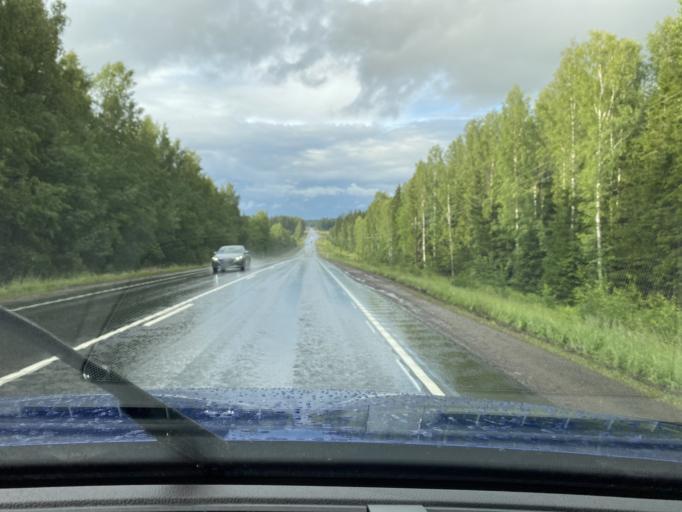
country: FI
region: Uusimaa
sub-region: Helsinki
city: Nurmijaervi
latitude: 60.4655
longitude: 24.8363
